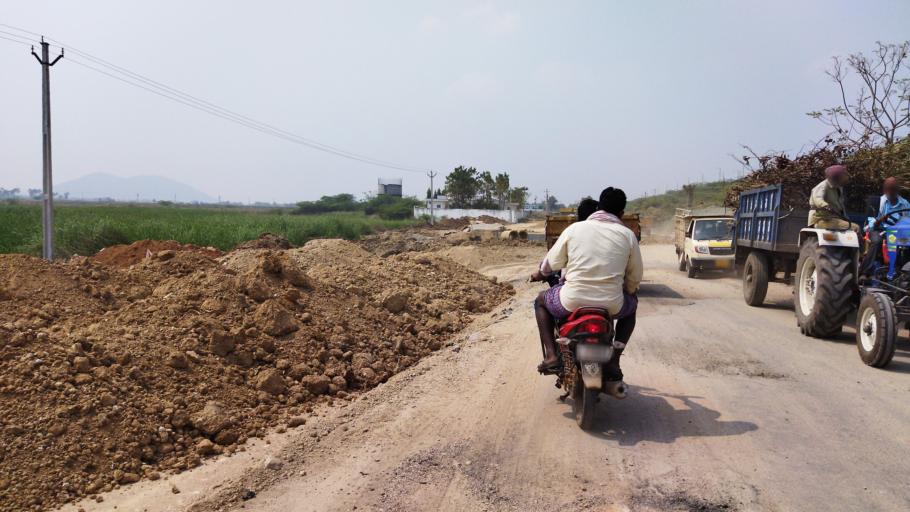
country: IN
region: Telangana
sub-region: Nalgonda
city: Nalgonda
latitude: 17.0792
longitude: 79.3061
